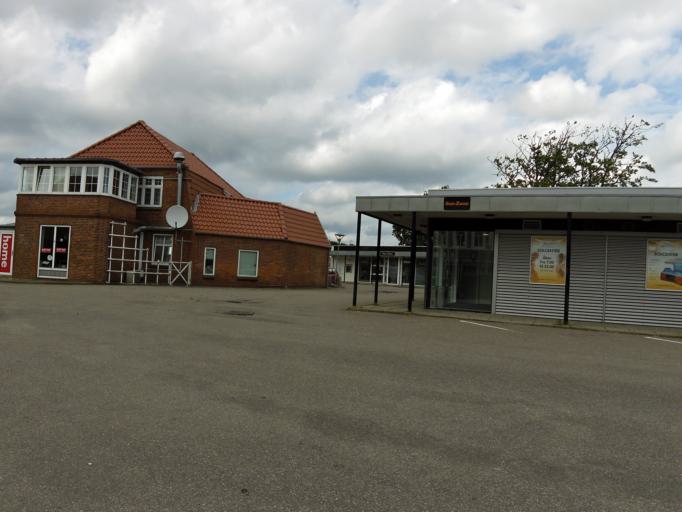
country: DK
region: South Denmark
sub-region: Aabenraa Kommune
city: Rodekro
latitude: 55.0702
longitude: 9.3358
